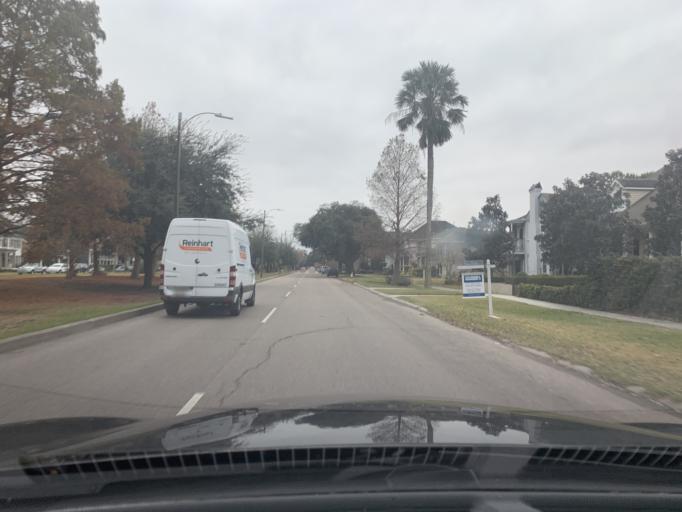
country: US
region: Louisiana
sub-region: Jefferson Parish
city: Metairie
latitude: 30.0140
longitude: -90.1071
